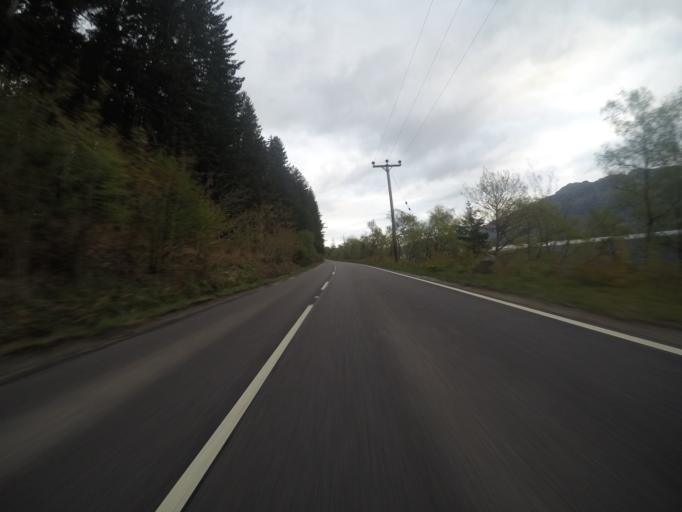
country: GB
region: Scotland
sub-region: Highland
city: Beauly
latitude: 57.1671
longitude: -4.6493
